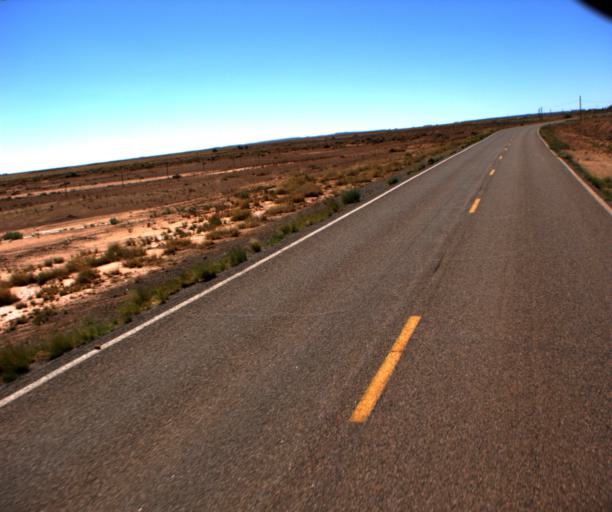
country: US
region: Arizona
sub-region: Coconino County
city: LeChee
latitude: 35.1497
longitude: -110.8971
